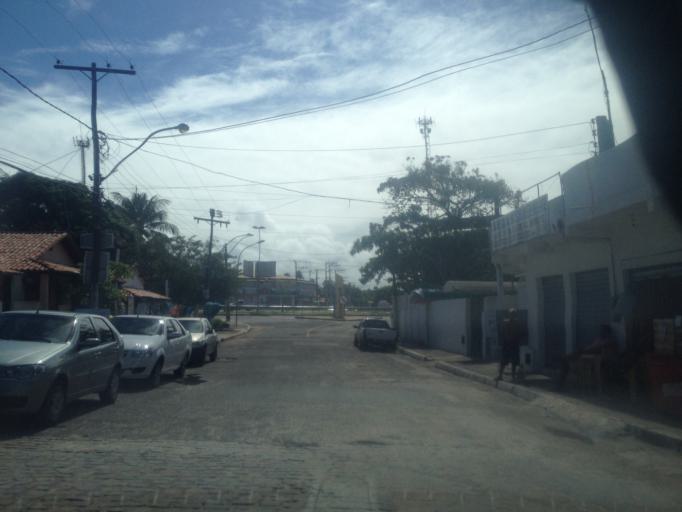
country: BR
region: Bahia
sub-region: Camacari
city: Camacari
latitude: -12.7038
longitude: -38.1335
